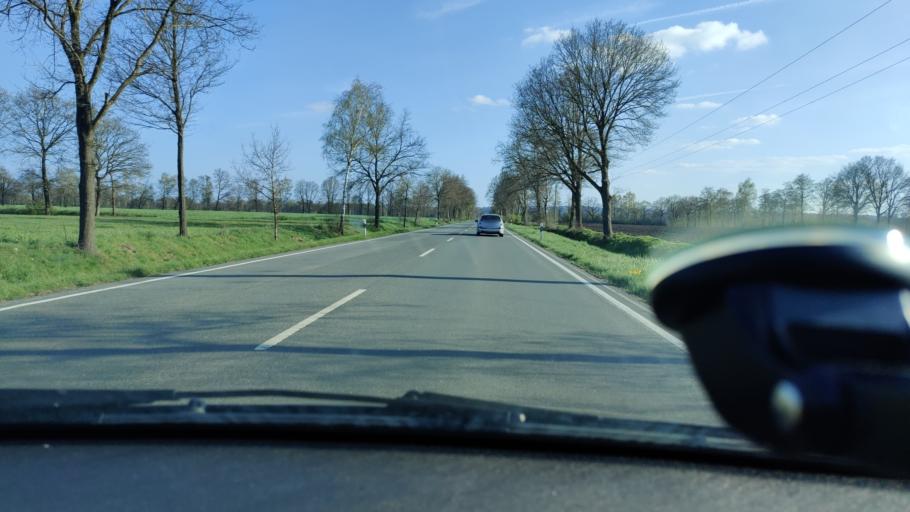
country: DE
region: North Rhine-Westphalia
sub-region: Regierungsbezirk Munster
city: Velen
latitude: 51.8763
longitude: 7.0510
